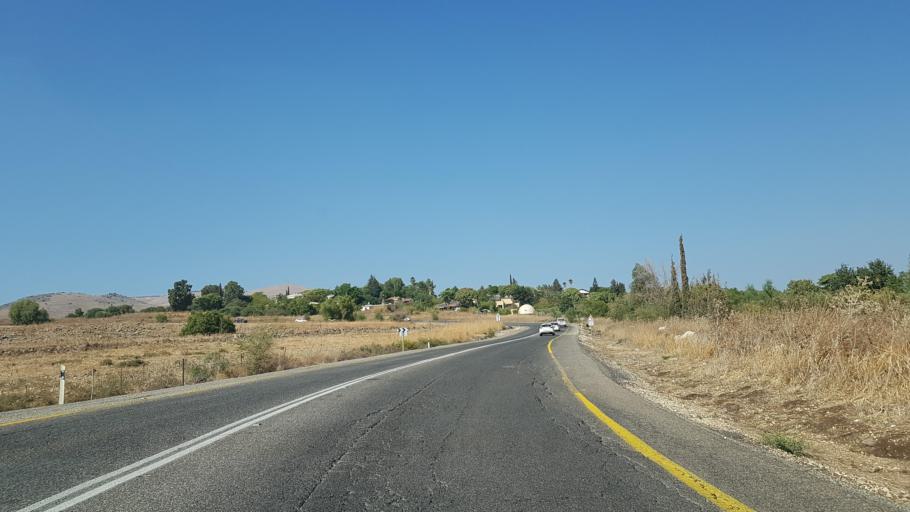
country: IL
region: Northern District
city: Rosh Pinna
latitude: 32.9075
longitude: 35.5495
